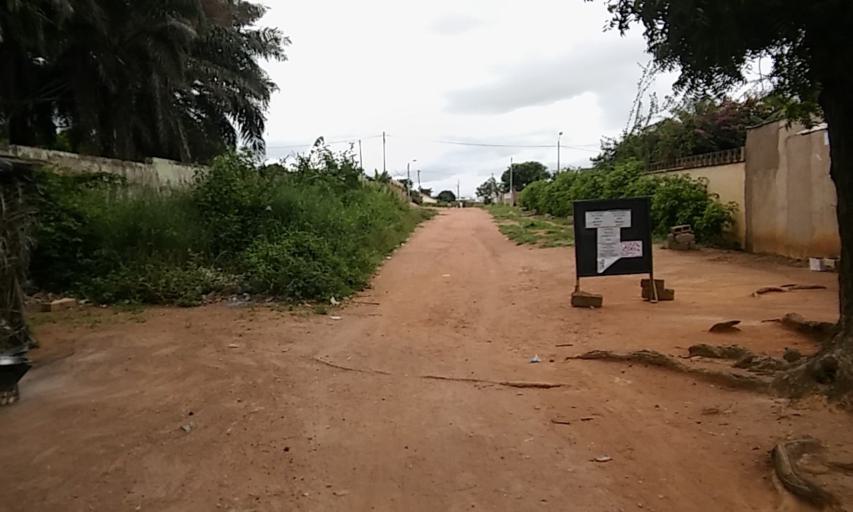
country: CI
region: Vallee du Bandama
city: Bouake
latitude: 7.6933
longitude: -5.0602
